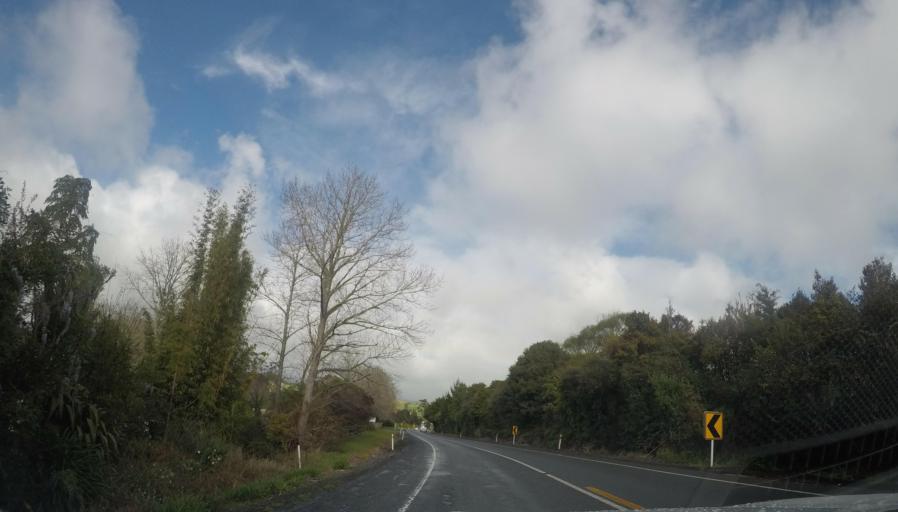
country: NZ
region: Auckland
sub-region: Auckland
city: Warkworth
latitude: -36.3978
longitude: 174.7058
